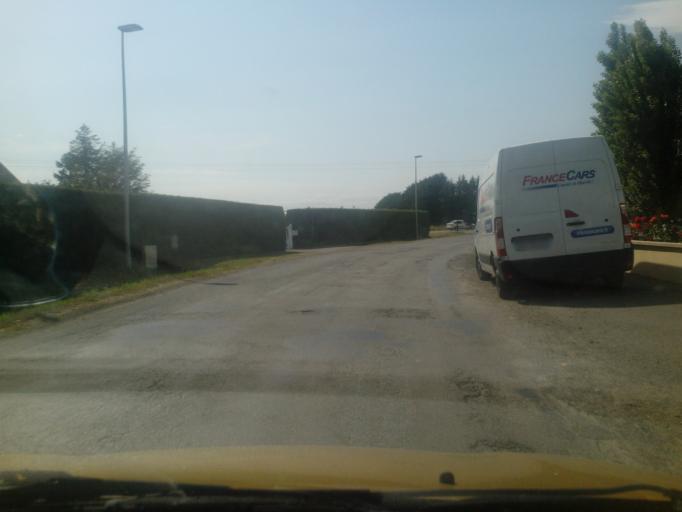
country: FR
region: Brittany
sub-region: Departement d'Ille-et-Vilaine
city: Melesse
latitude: 48.2303
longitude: -1.7052
